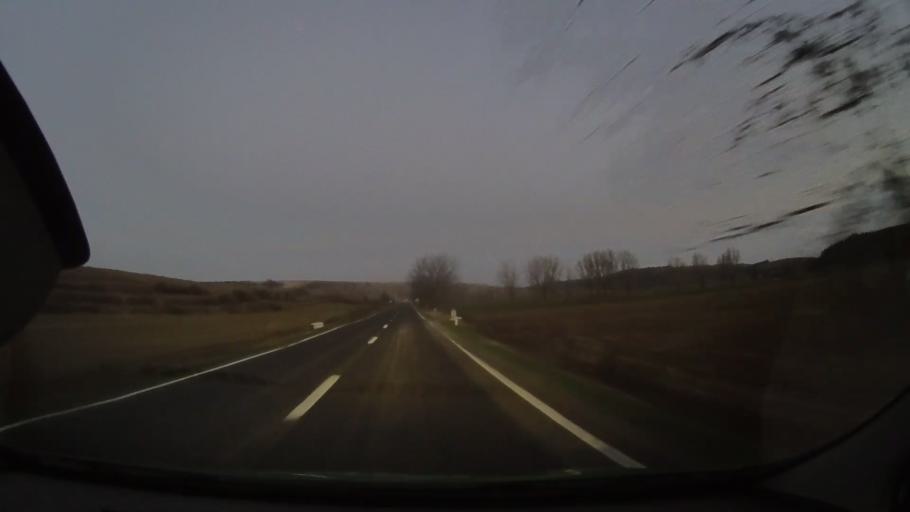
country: RO
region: Constanta
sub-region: Comuna Ion Corvin
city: Ion Corvin
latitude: 44.1027
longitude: 27.7914
